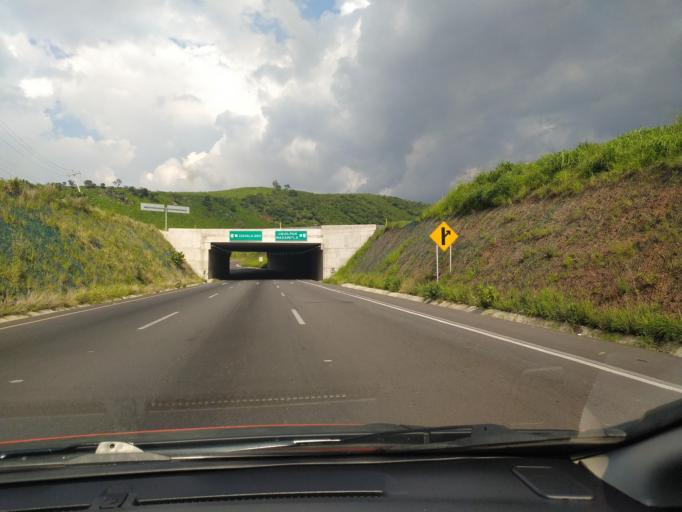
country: MX
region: Jalisco
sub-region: Acatlan de Juarez
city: Villa de los Ninos
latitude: 20.4233
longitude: -103.5557
